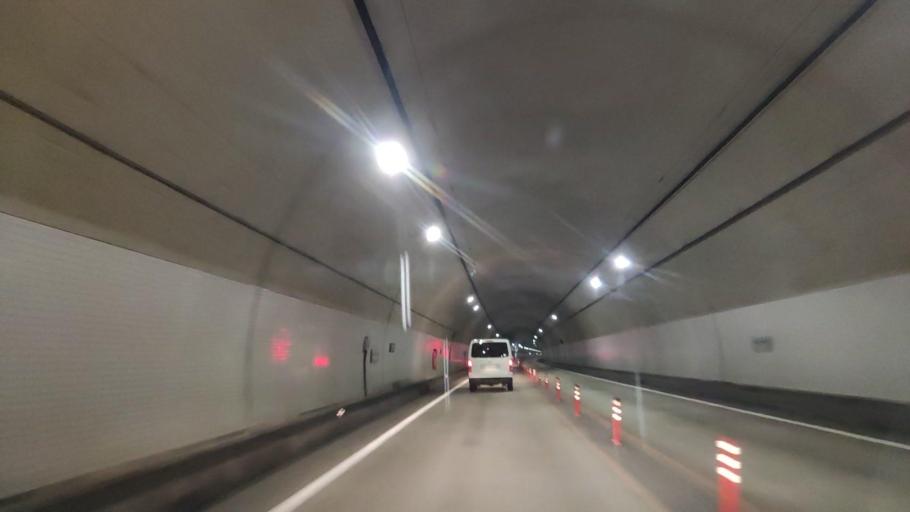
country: JP
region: Akita
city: Odate
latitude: 40.3432
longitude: 140.6551
